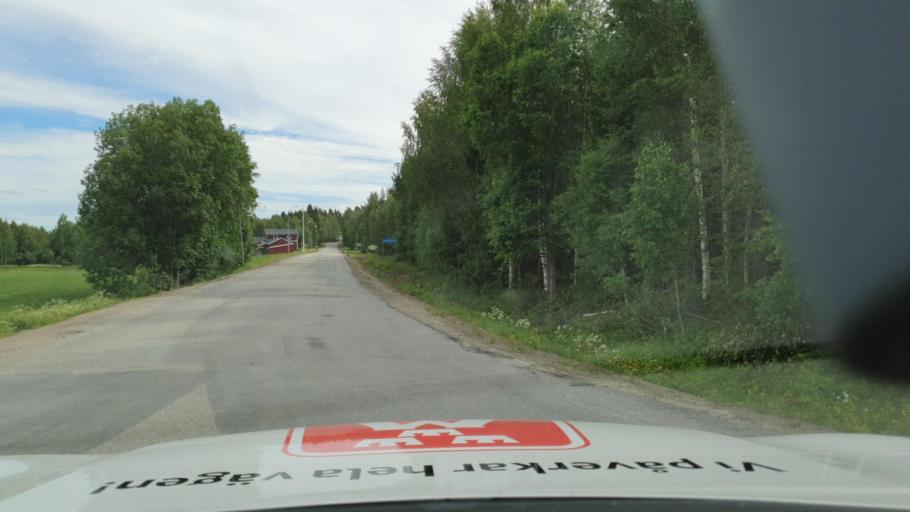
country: SE
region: Vaesterbotten
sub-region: Robertsfors Kommun
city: Robertsfors
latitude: 64.4121
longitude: 21.0006
